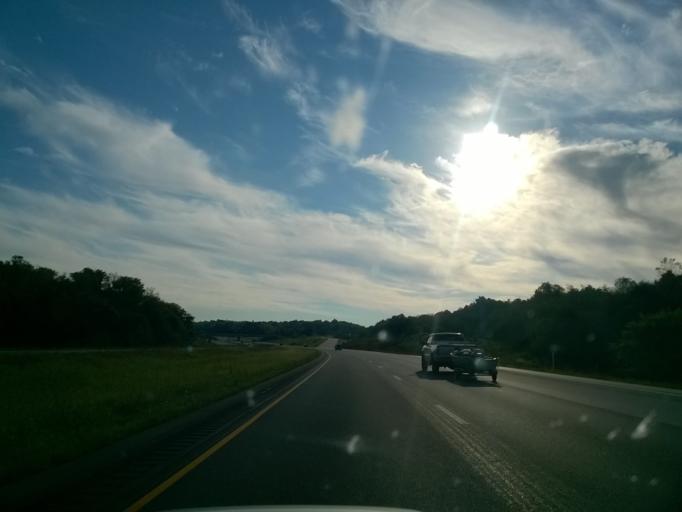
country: US
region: Indiana
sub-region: Warrick County
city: Boonville
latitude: 38.1923
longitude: -87.2993
